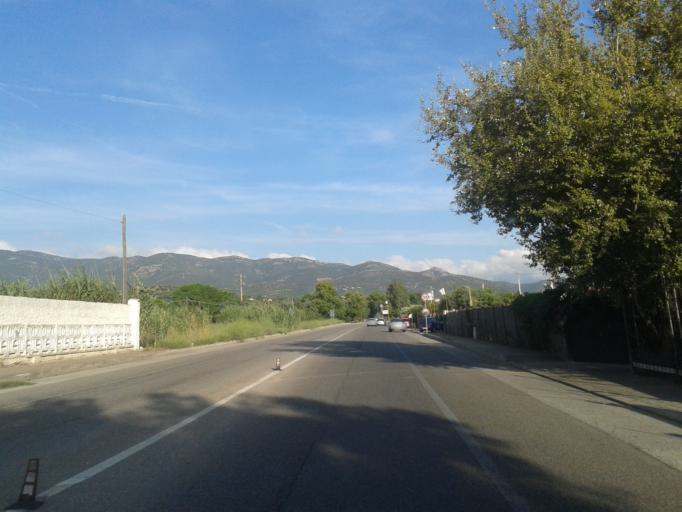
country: IT
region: Sardinia
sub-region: Provincia di Cagliari
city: Quartu Sant'Elena
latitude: 39.2187
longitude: 9.2960
